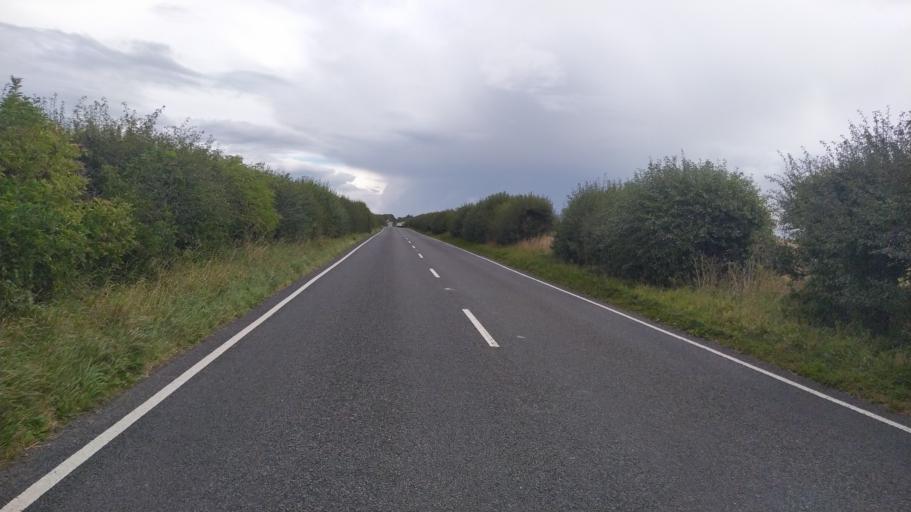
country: GB
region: England
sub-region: Wiltshire
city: Bower Chalke
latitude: 50.9405
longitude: -1.9976
